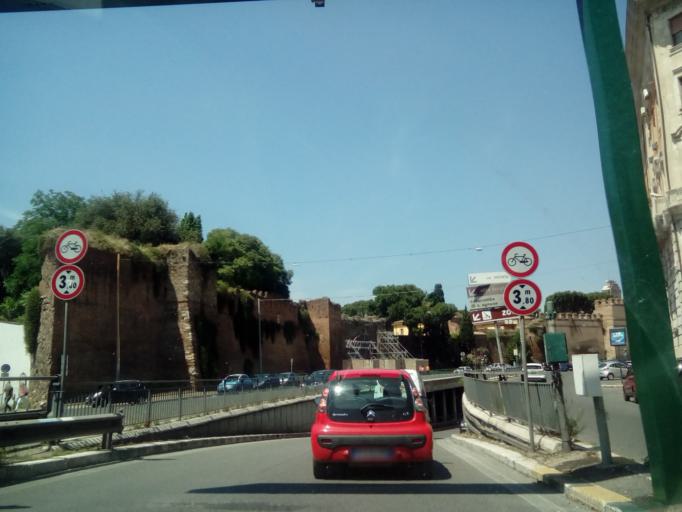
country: IT
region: Latium
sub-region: Citta metropolitana di Roma Capitale
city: Rome
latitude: 41.9083
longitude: 12.5041
